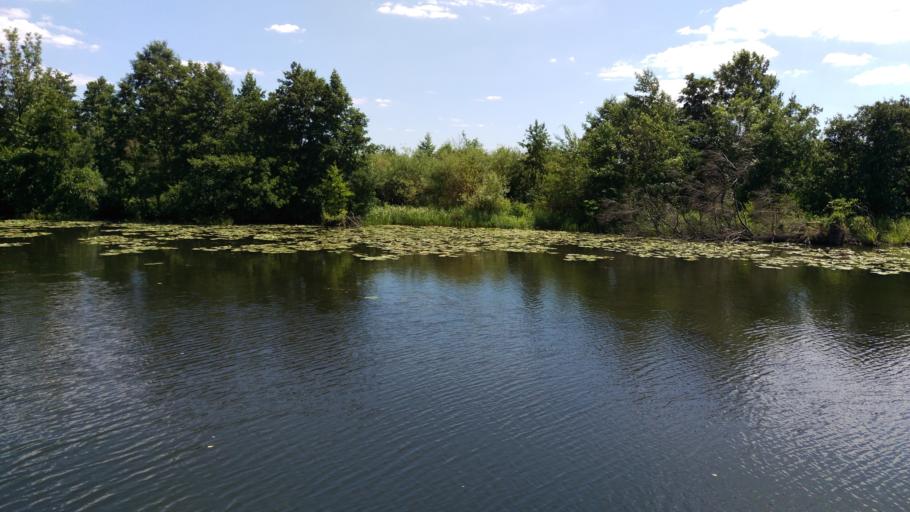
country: DE
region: Brandenburg
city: Brandenburg an der Havel
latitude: 52.4142
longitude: 12.5731
